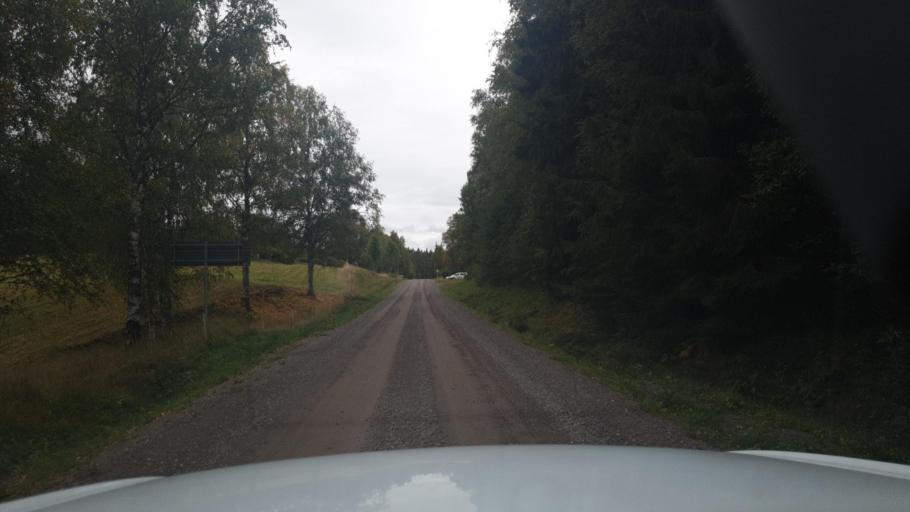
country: SE
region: Vaermland
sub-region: Eda Kommun
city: Charlottenberg
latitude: 60.0601
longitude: 12.5511
